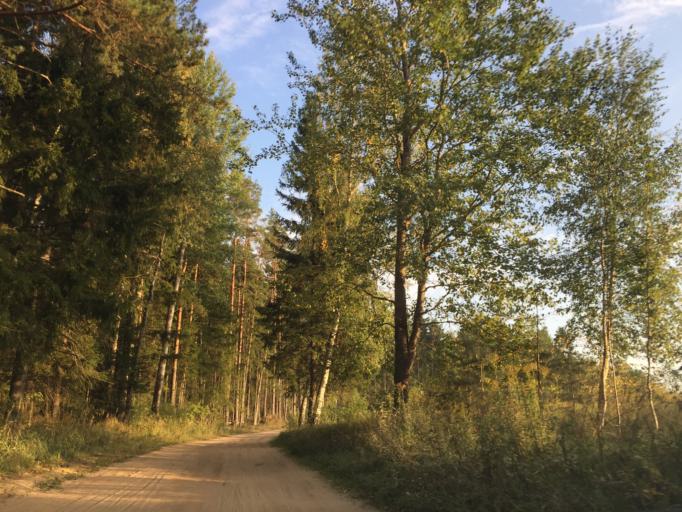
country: LV
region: Baldone
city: Baldone
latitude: 56.7620
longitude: 24.4092
